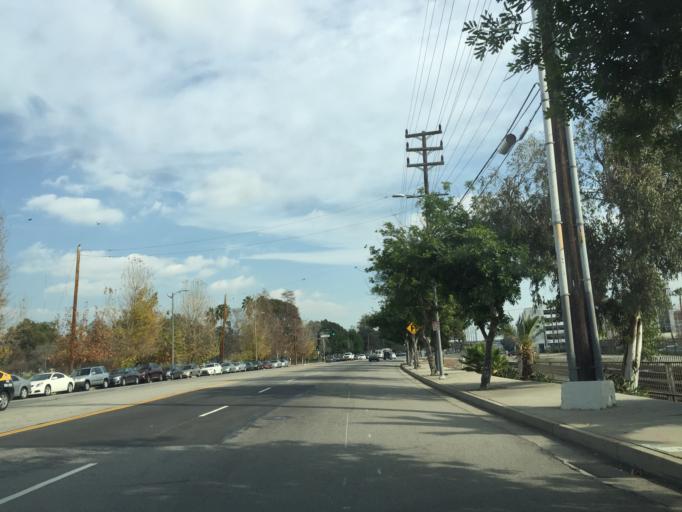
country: US
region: California
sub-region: Los Angeles County
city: Boyle Heights
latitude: 34.0656
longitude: -118.2039
